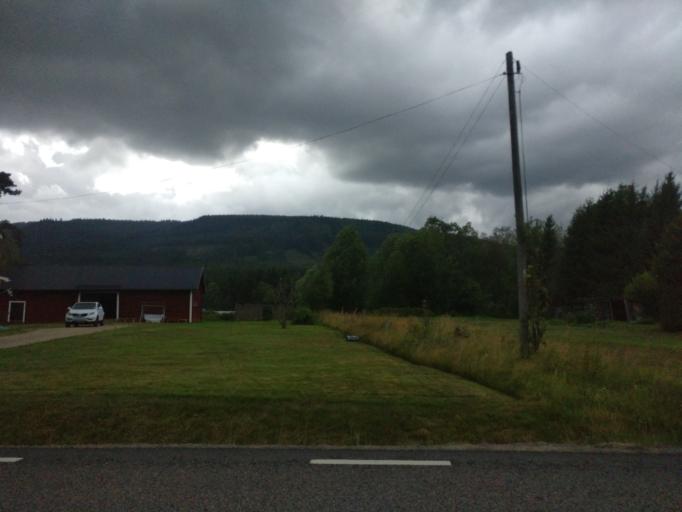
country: SE
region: Vaermland
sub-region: Torsby Kommun
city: Torsby
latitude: 60.7338
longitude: 12.8672
